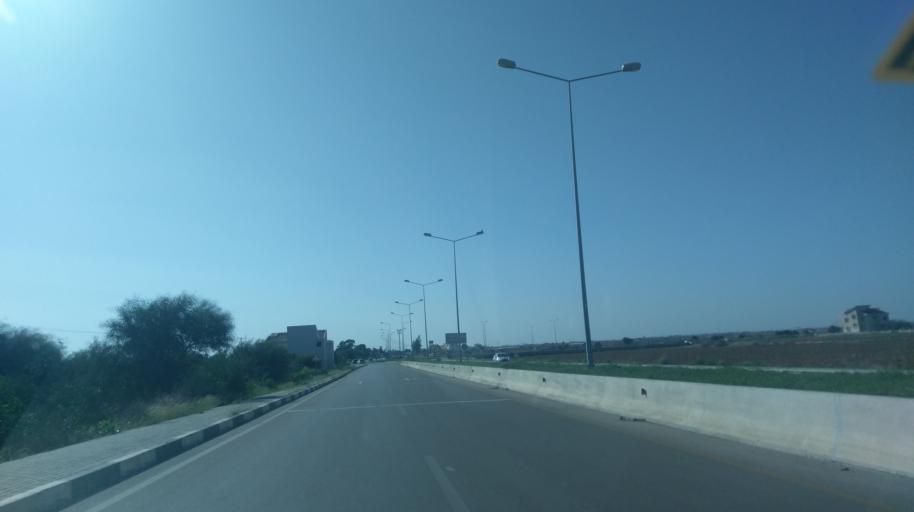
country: CY
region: Ammochostos
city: Trikomo
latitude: 35.2318
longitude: 33.8989
